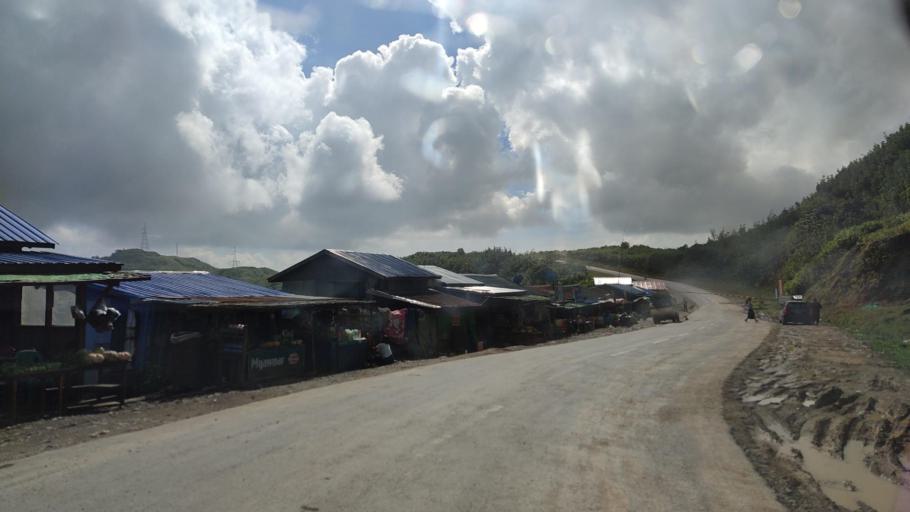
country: MM
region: Magway
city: Minbu
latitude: 19.8338
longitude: 94.2854
